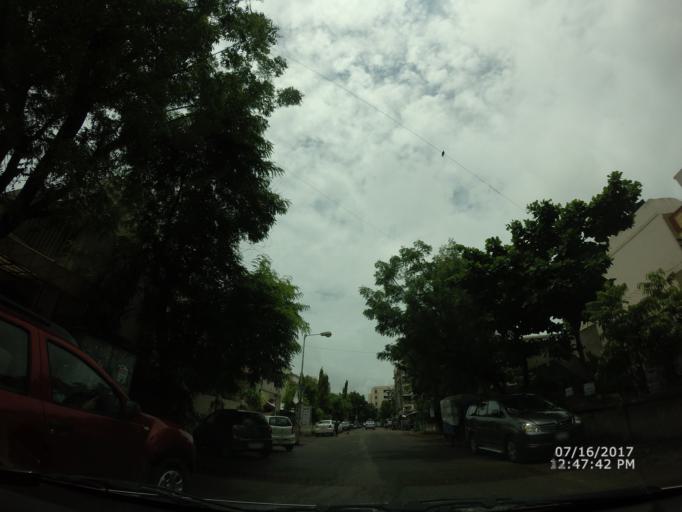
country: IN
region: Gujarat
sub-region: Ahmadabad
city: Sarkhej
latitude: 23.0184
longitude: 72.5127
